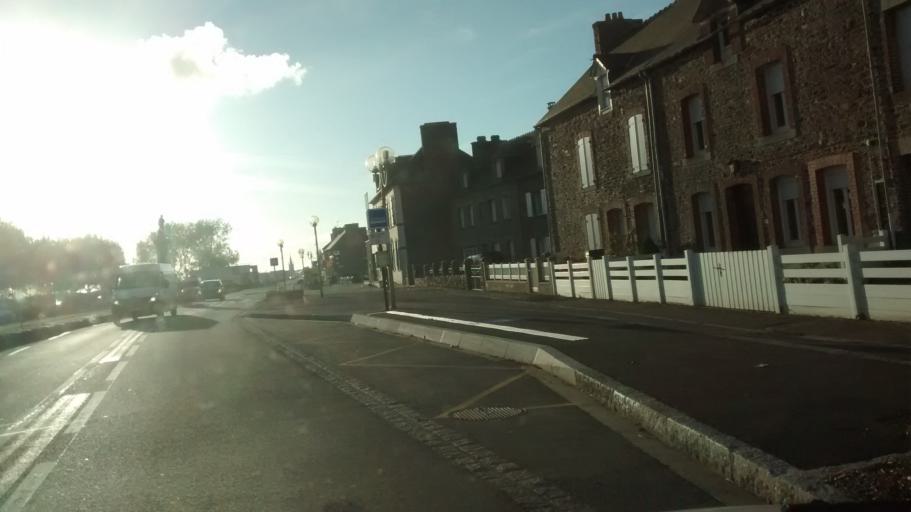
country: FR
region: Brittany
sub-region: Departement d'Ille-et-Vilaine
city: La Fresnais
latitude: 48.6198
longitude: -1.8511
